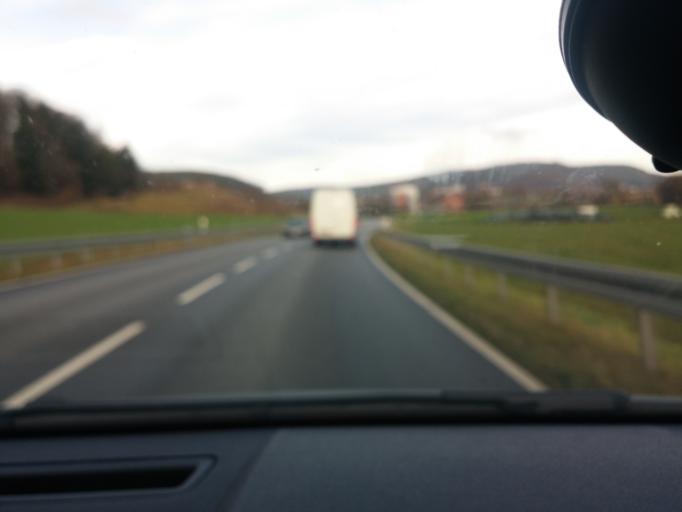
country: DE
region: Hesse
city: Hochst im Odenwald
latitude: 49.7865
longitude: 8.9900
